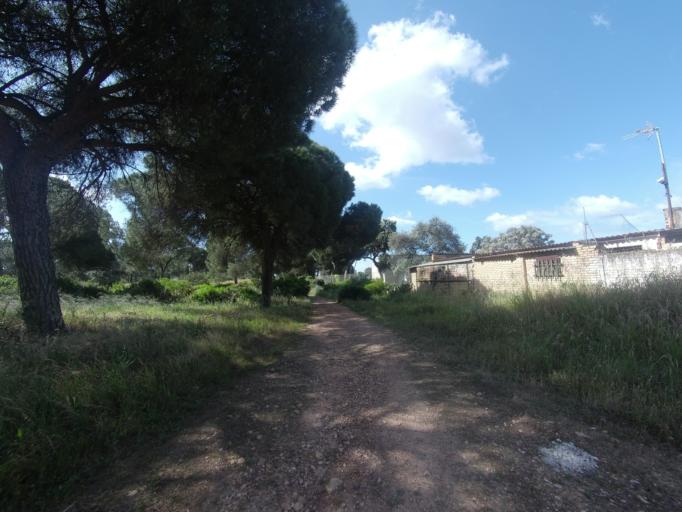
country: ES
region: Andalusia
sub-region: Provincia de Huelva
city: Aljaraque
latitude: 37.2441
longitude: -7.0305
